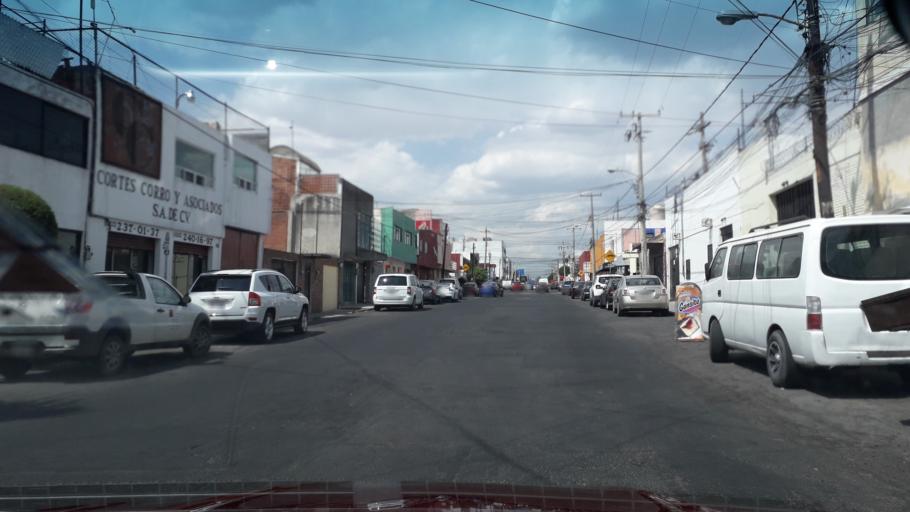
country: MX
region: Puebla
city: Puebla
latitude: 19.0411
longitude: -98.2199
